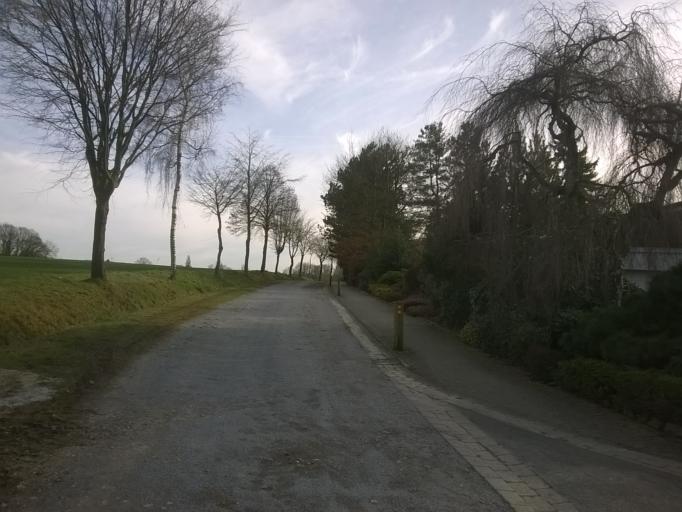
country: DE
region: North Rhine-Westphalia
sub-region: Regierungsbezirk Detmold
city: Hiddenhausen
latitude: 52.1704
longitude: 8.6189
